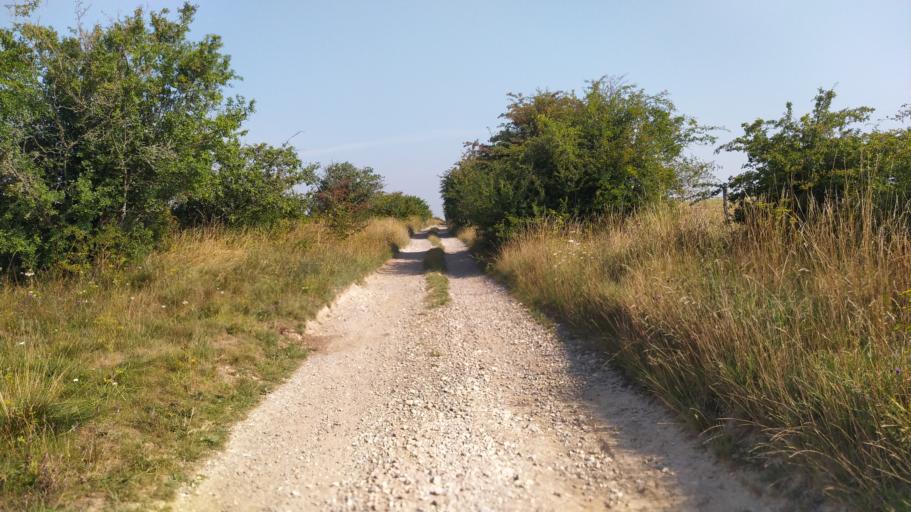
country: GB
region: England
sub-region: Wiltshire
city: Shrewton
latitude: 51.1709
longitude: -1.9521
